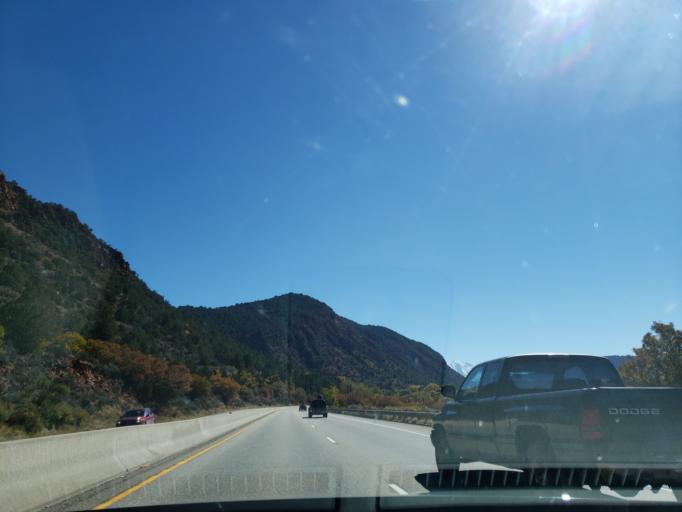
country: US
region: Colorado
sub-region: Garfield County
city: Glenwood Springs
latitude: 39.5110
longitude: -107.3068
